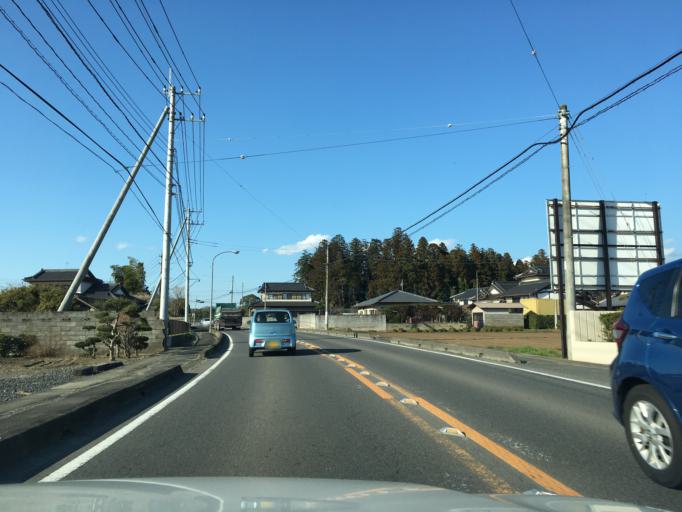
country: JP
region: Ibaraki
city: Omiya
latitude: 36.5932
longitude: 140.4118
